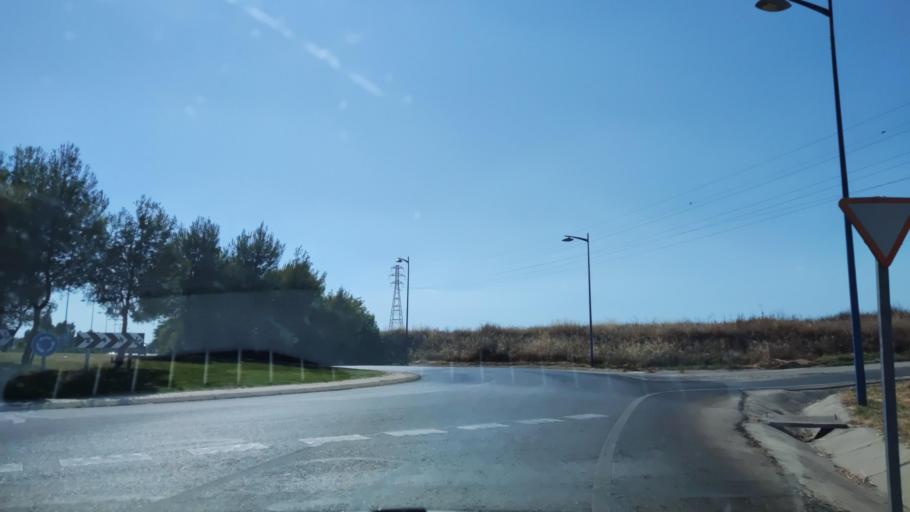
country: ES
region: Madrid
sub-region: Provincia de Madrid
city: Leganes
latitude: 40.3463
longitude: -3.7752
